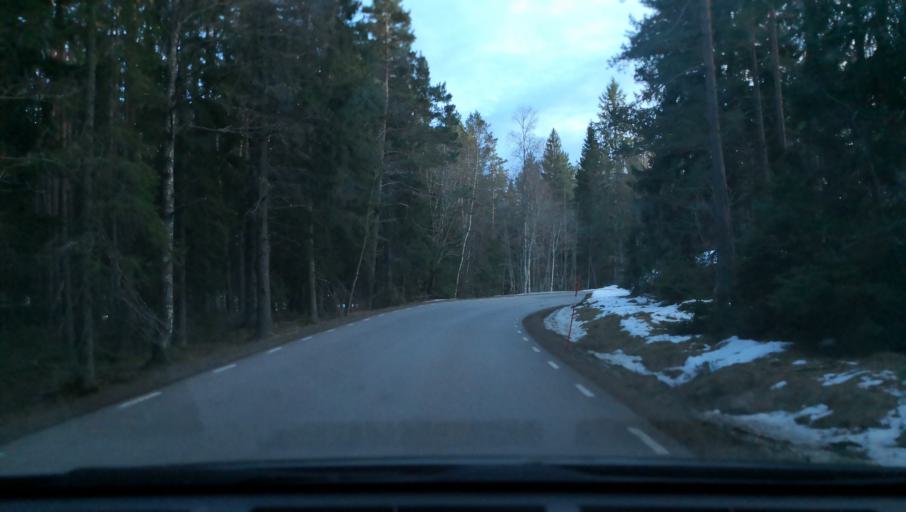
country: SE
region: Uppsala
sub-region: Osthammars Kommun
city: Osterbybruk
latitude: 60.2231
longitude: 17.9187
